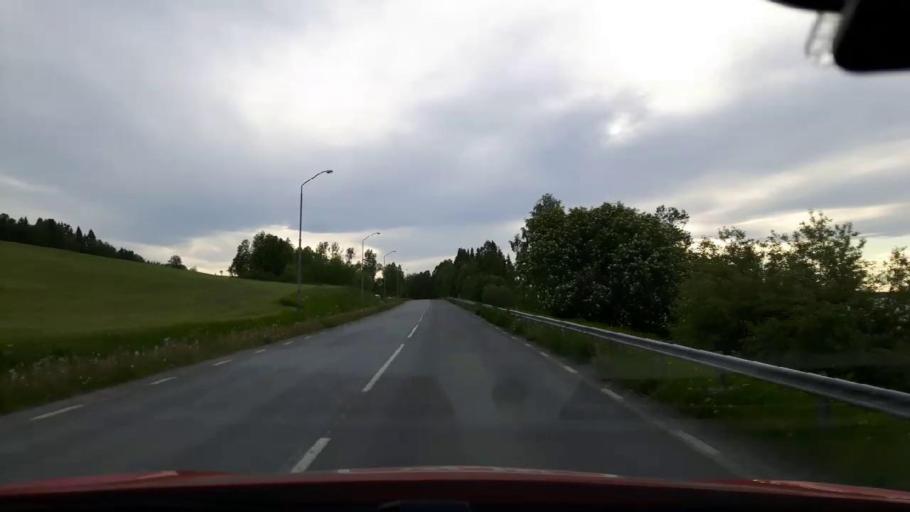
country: SE
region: Jaemtland
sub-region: OEstersunds Kommun
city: Ostersund
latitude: 63.1552
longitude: 14.5203
